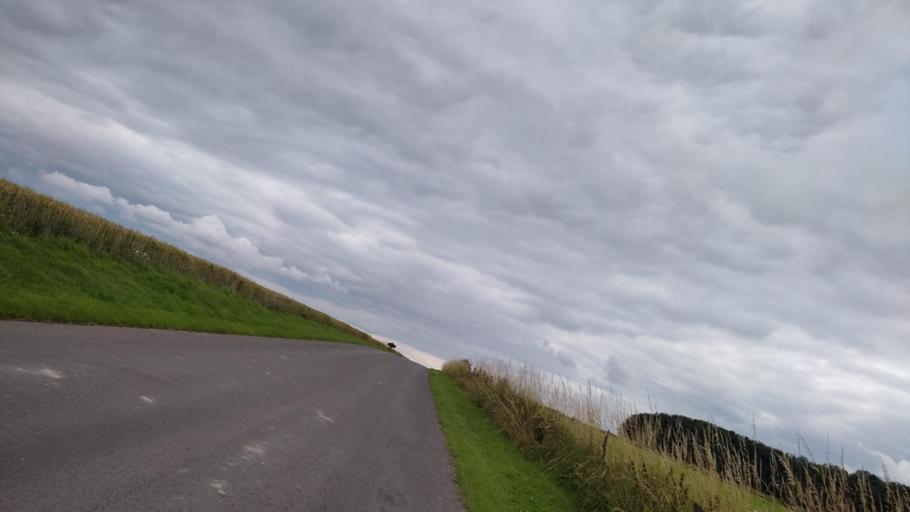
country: FR
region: Nord-Pas-de-Calais
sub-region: Departement du Pas-de-Calais
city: Beaumetz-les-Loges
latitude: 50.2365
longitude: 2.6288
